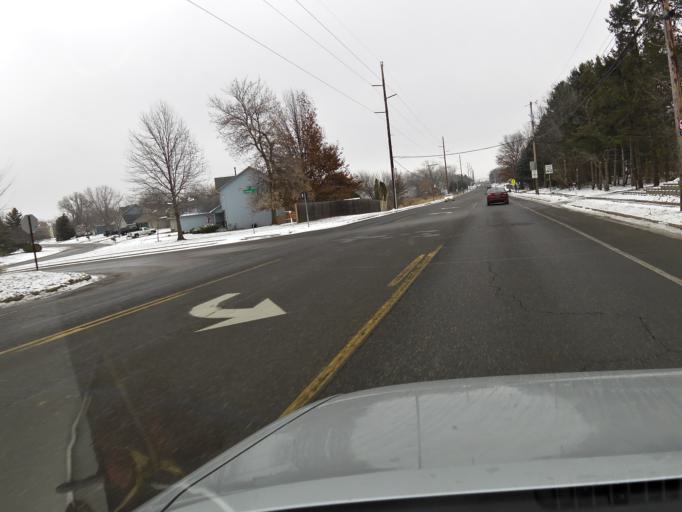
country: US
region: Minnesota
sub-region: Washington County
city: Oakdale
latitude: 44.9631
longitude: -92.9750
